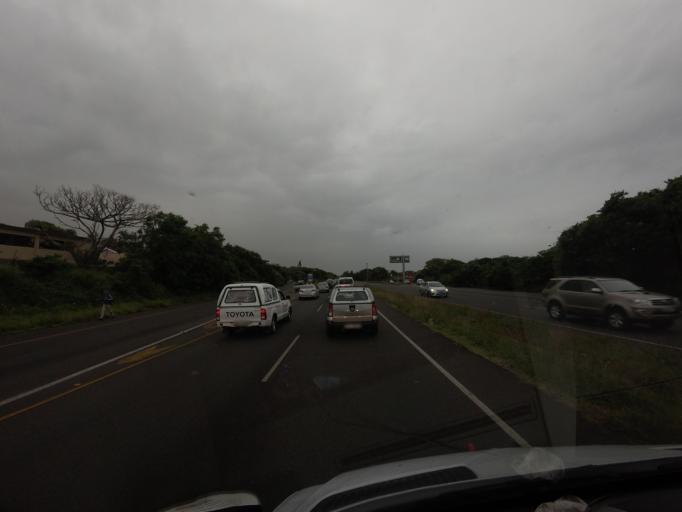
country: ZA
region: KwaZulu-Natal
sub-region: eThekwini Metropolitan Municipality
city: Durban
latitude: -29.7185
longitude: 31.0872
